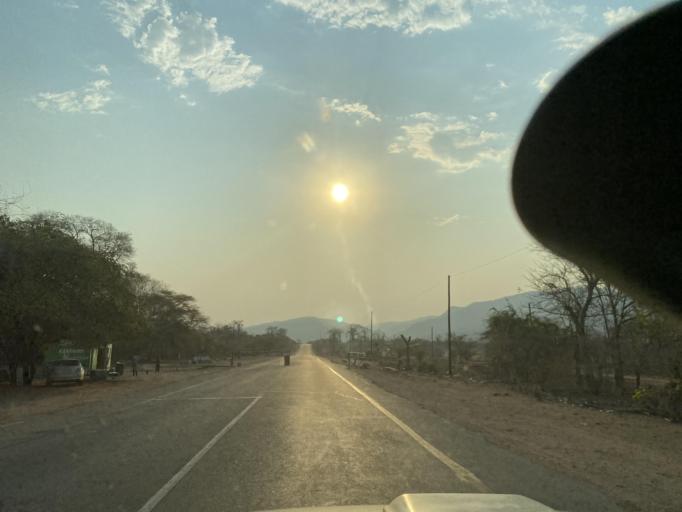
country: ZW
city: Chirundu
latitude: -16.0186
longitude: 28.6238
